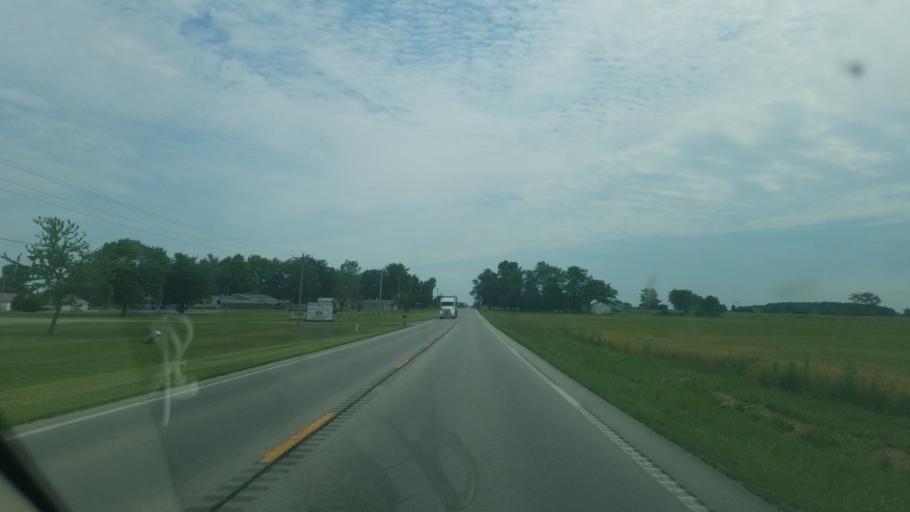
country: US
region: Ohio
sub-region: Seneca County
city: Fostoria
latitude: 41.1273
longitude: -83.4765
